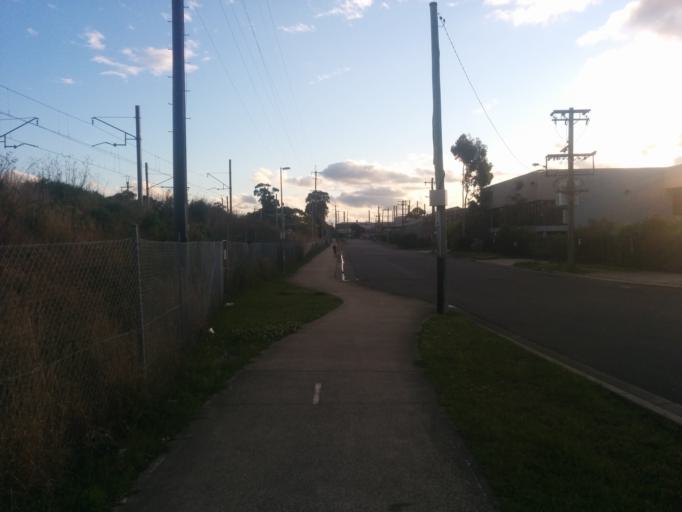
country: AU
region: New South Wales
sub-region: Fairfield
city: Fairfield East
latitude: -33.8630
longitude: 150.9735
